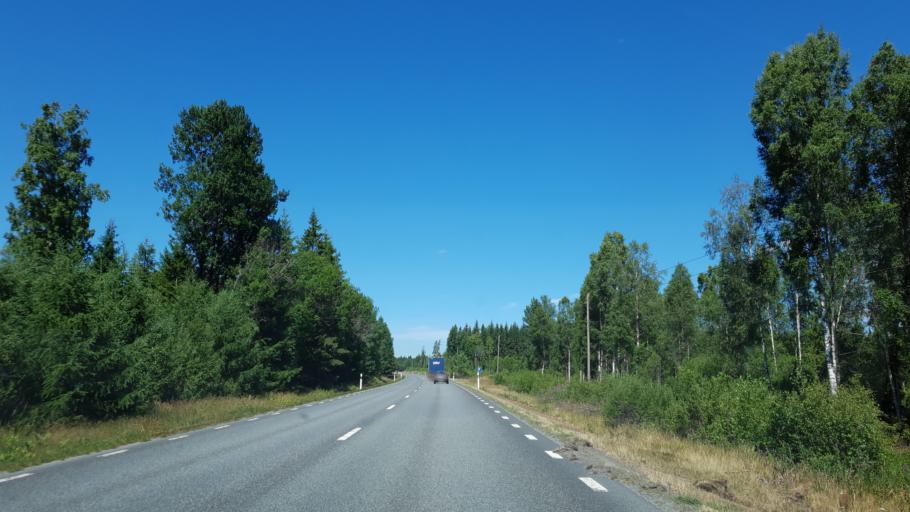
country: SE
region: Joenkoeping
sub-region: Varnamo Kommun
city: Rydaholm
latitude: 57.0408
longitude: 14.2383
